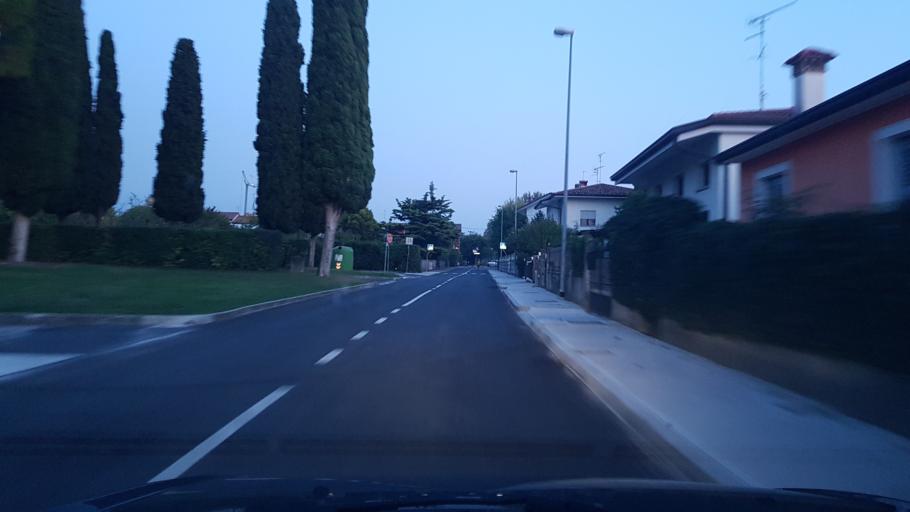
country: IT
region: Friuli Venezia Giulia
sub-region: Provincia di Gorizia
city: Staranzano
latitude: 45.8081
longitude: 13.4983
